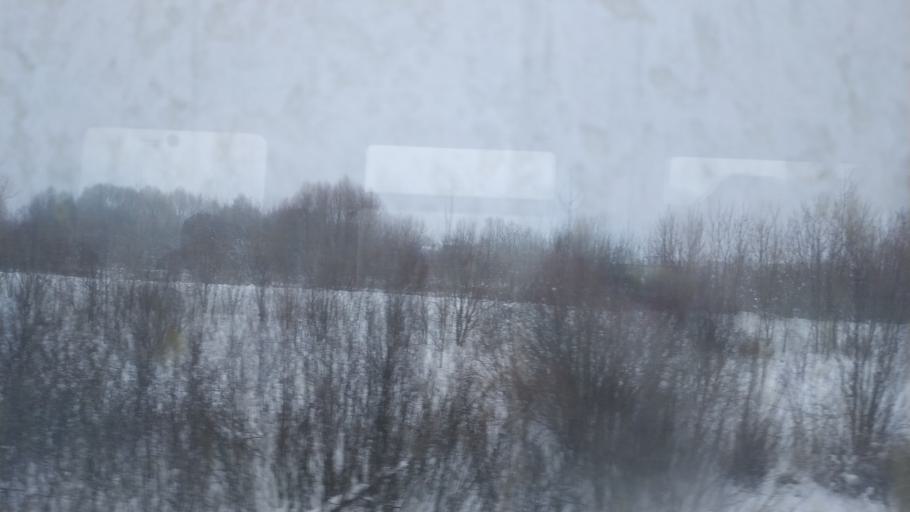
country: RU
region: Moskovskaya
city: Ramenskoye
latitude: 55.5475
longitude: 38.2759
